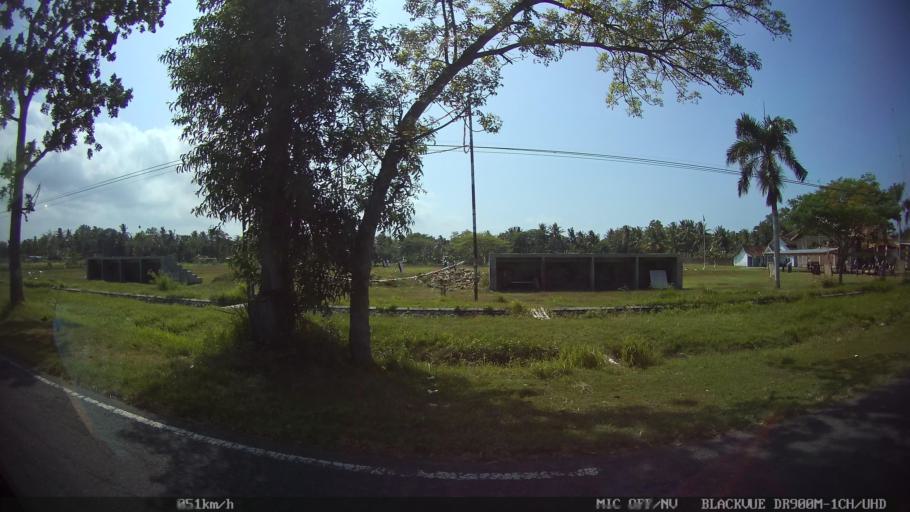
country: ID
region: Daerah Istimewa Yogyakarta
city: Srandakan
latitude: -7.9051
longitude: 110.1524
